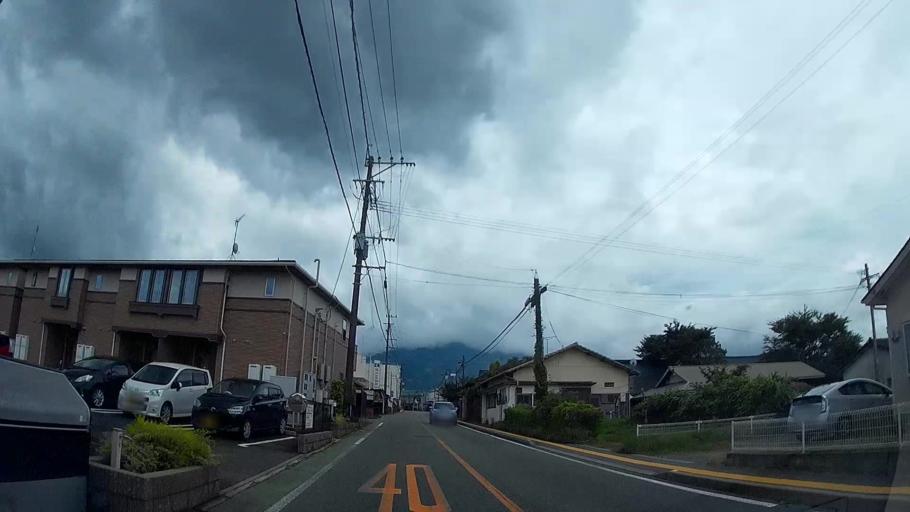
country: JP
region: Kumamoto
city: Aso
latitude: 32.9431
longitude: 131.1177
